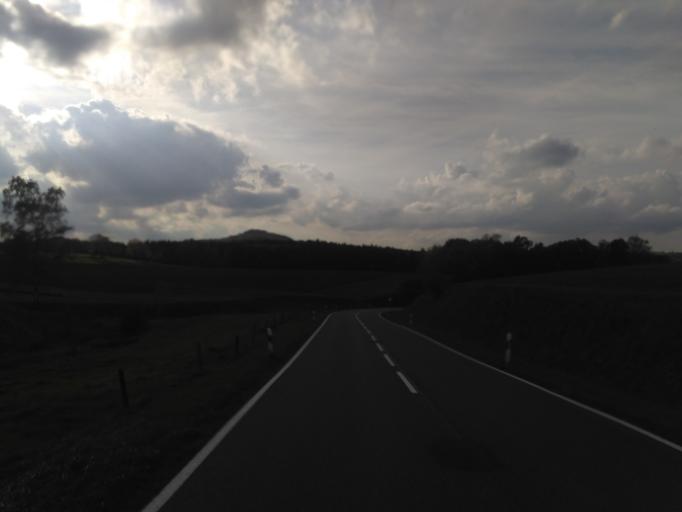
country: DE
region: Saxony
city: Neustadt in Sachsen
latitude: 50.9667
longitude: 14.1994
